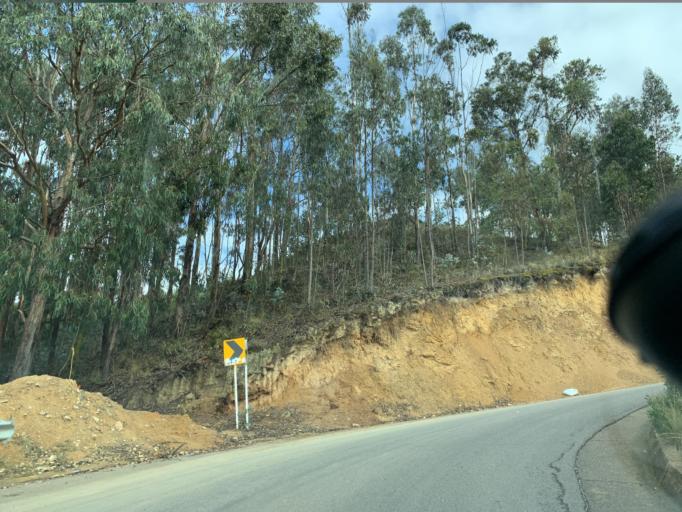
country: CO
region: Boyaca
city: Tunja
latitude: 5.5646
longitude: -73.3629
